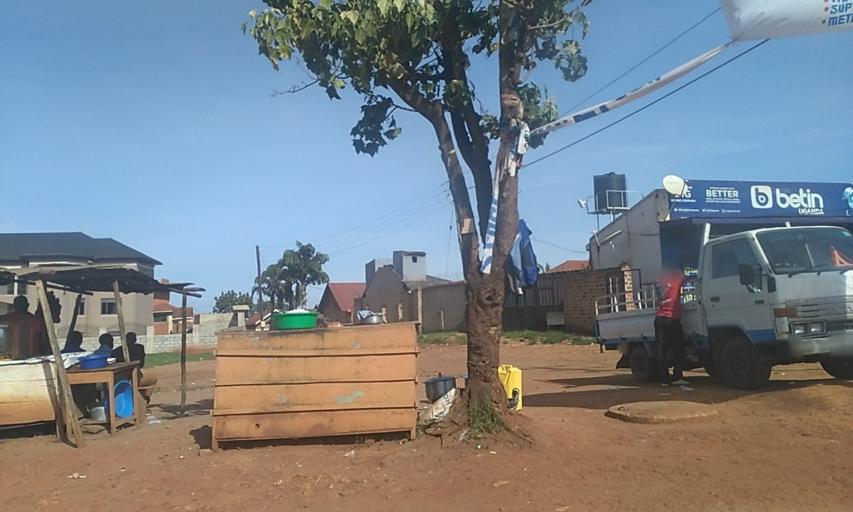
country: UG
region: Central Region
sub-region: Wakiso District
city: Kireka
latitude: 0.3715
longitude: 32.6241
